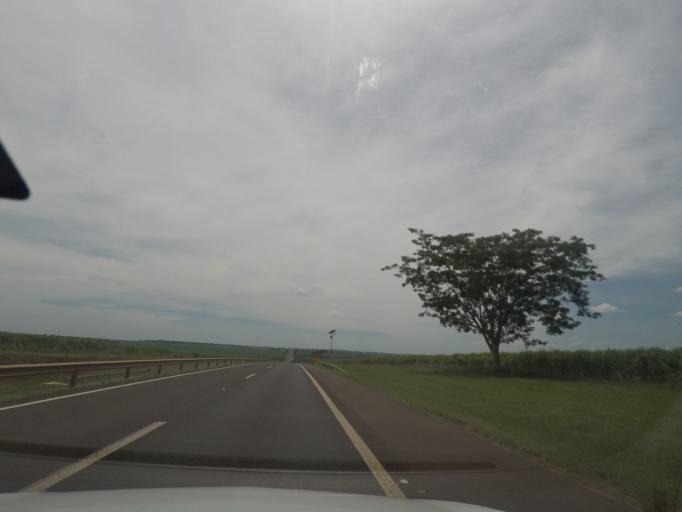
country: BR
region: Sao Paulo
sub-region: Bebedouro
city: Bebedouro
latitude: -21.0454
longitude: -48.4161
